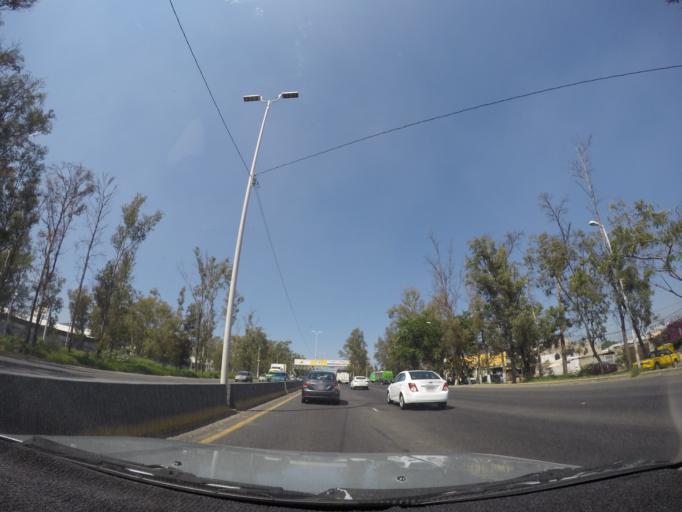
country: MX
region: Jalisco
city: Las Pintas de Arriba
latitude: 20.5924
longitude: -103.3210
